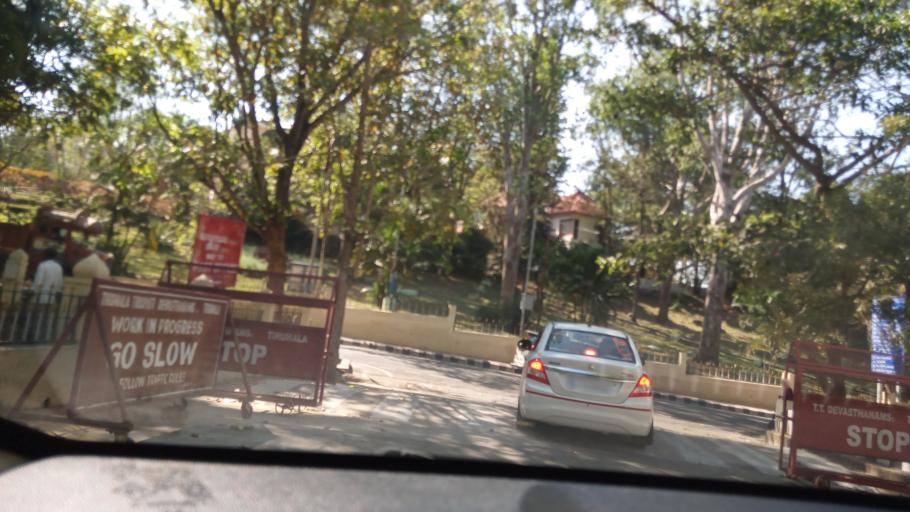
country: IN
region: Andhra Pradesh
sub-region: Chittoor
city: Tirumala
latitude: 13.6781
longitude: 79.3486
